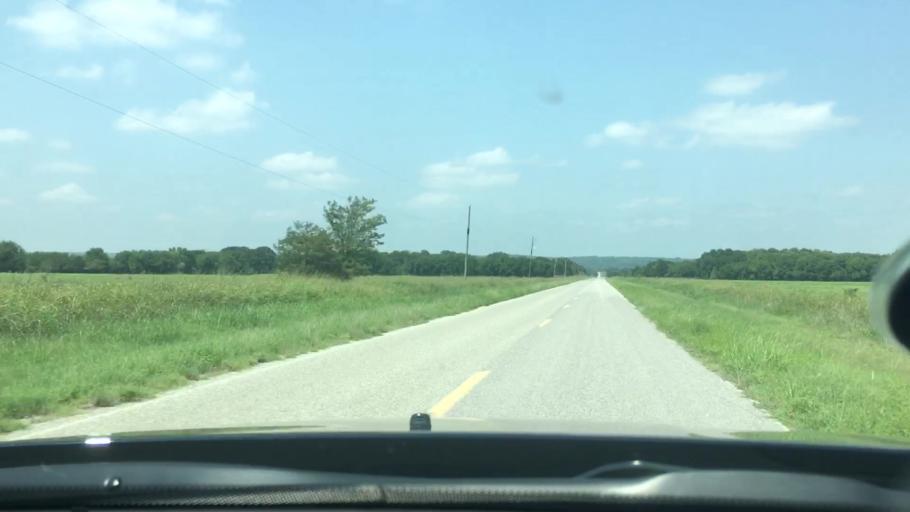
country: US
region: Oklahoma
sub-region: Johnston County
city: Tishomingo
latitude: 34.3807
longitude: -96.4962
